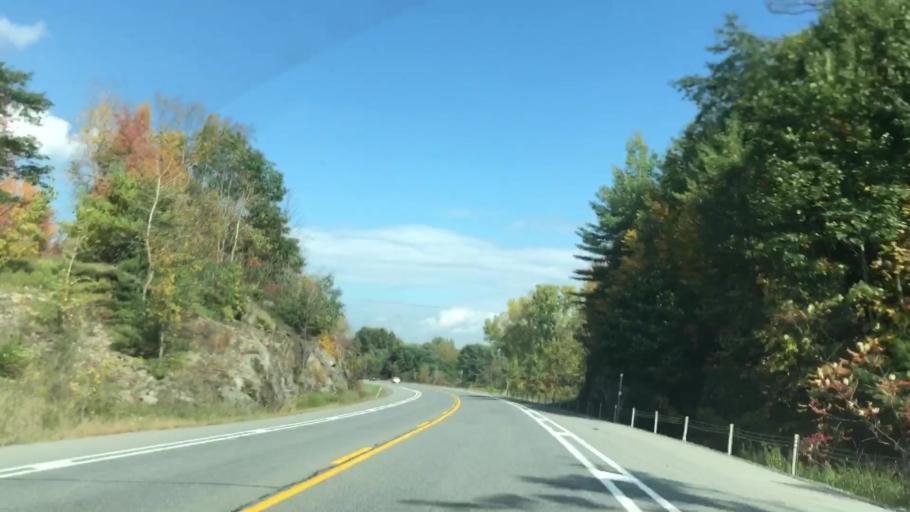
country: US
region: New York
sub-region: Washington County
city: Whitehall
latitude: 43.4711
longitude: -73.4343
